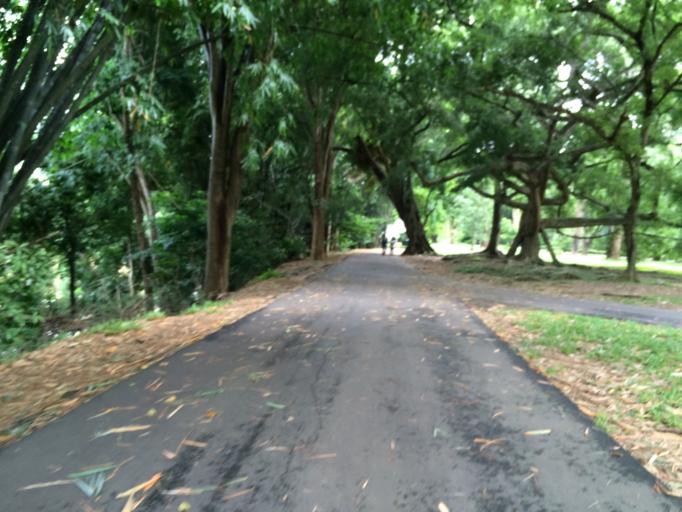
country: LK
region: Central
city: Kandy
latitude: 7.2746
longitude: 80.5929
